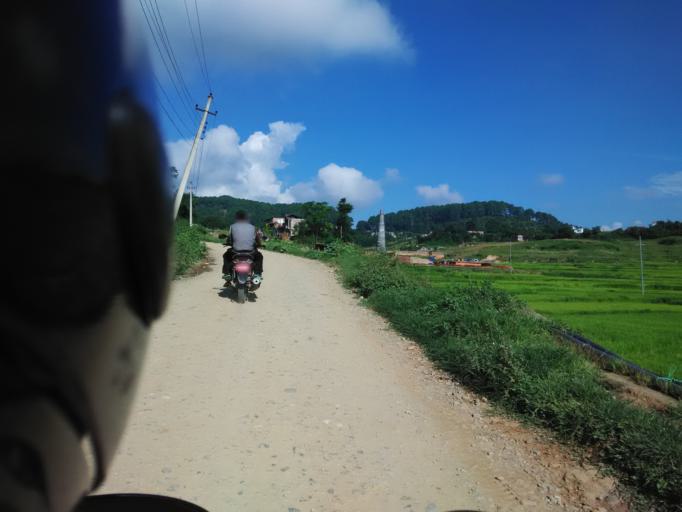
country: NP
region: Central Region
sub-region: Bagmati Zone
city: Patan
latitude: 27.6067
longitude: 85.3470
